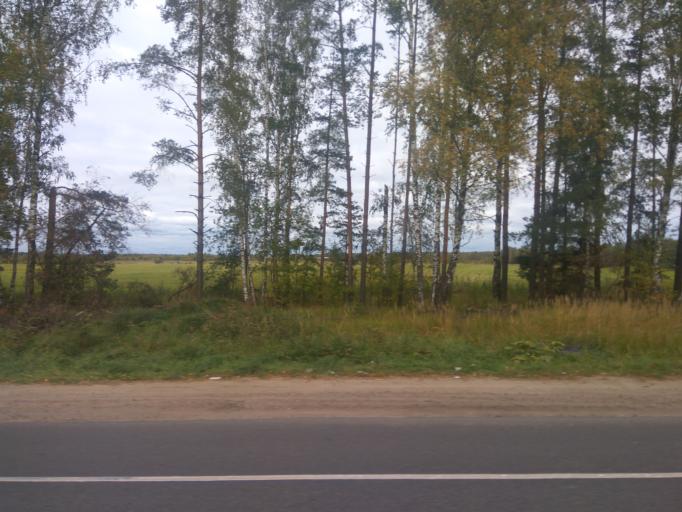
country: RU
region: Moskovskaya
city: Krasnoarmeysk
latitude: 56.0113
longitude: 38.1521
